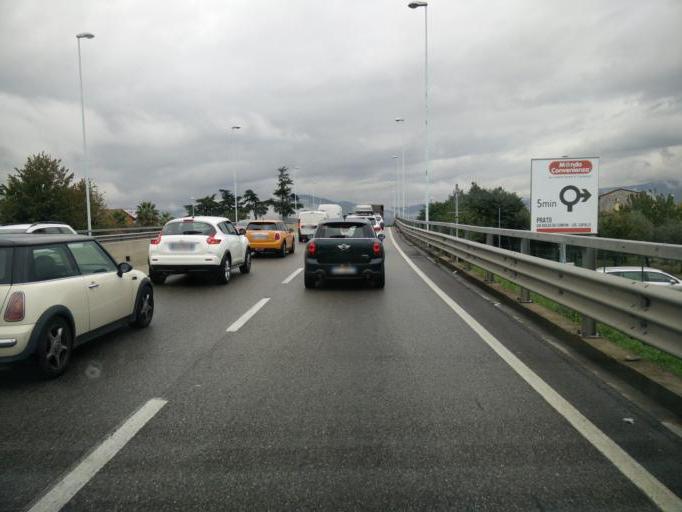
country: IT
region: Tuscany
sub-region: Provincia di Prato
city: Prato
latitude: 43.8767
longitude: 11.0624
